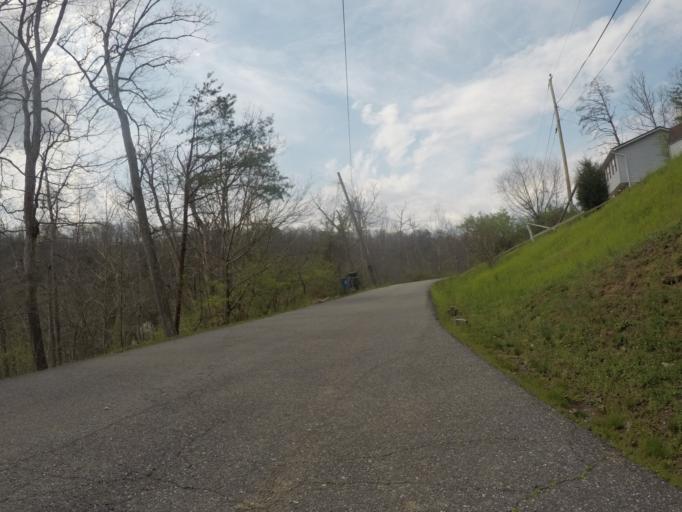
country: US
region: West Virginia
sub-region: Cabell County
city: Pea Ridge
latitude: 38.3978
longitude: -82.3352
